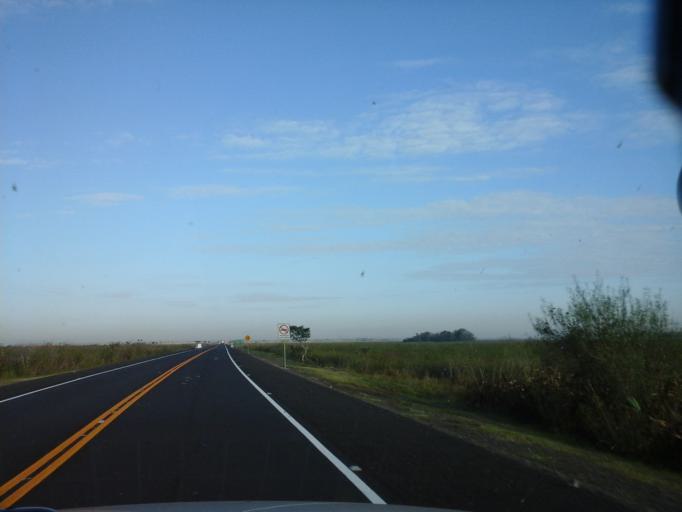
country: PY
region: Neembucu
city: Cerrito
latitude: -26.8939
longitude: -57.6981
